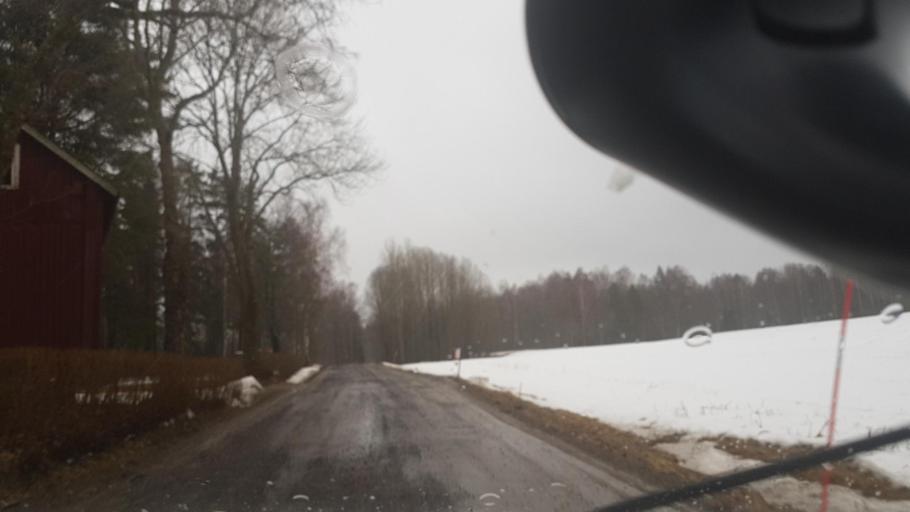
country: SE
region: Vaermland
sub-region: Eda Kommun
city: Amotfors
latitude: 59.8096
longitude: 12.3609
